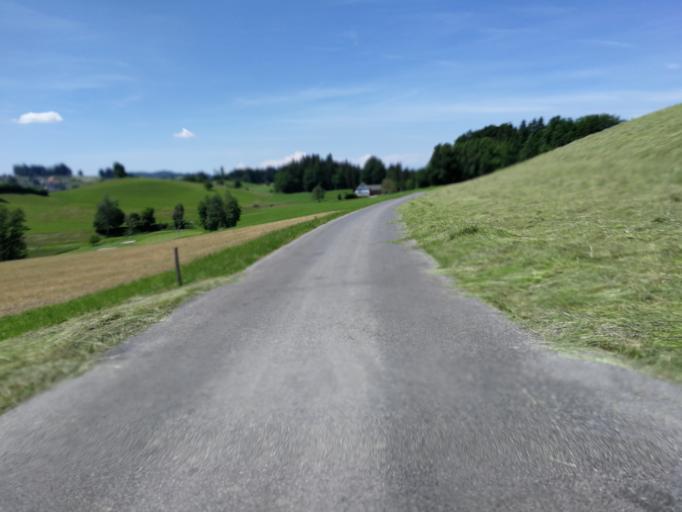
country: CH
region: Zurich
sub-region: Bezirk Horgen
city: Waedenswil / Hangenmoos
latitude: 47.2115
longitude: 8.6292
